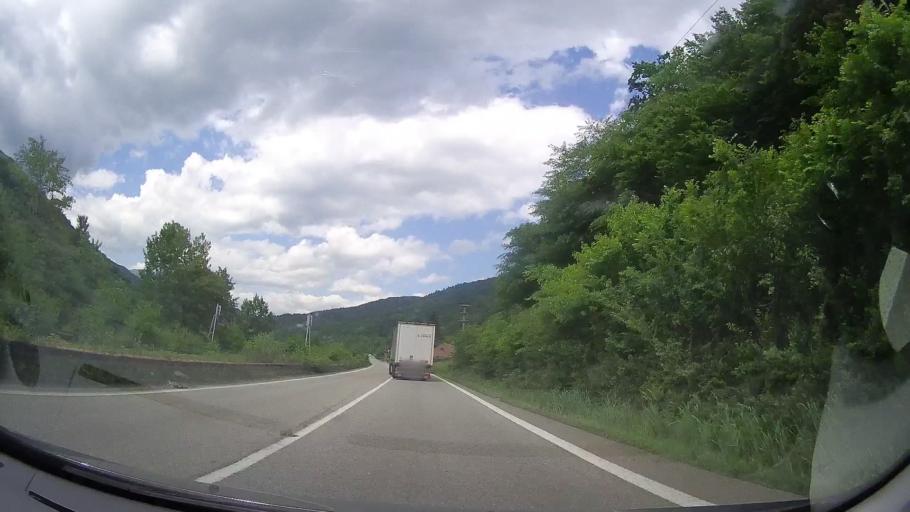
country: RO
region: Valcea
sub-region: Oras Calimanesti
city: Jiblea Veche
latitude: 45.2533
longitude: 24.3390
